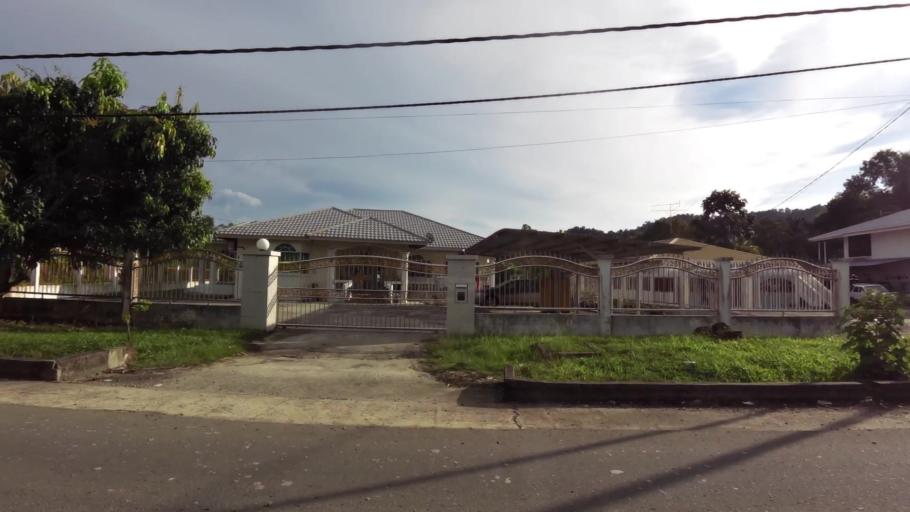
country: BN
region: Brunei and Muara
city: Bandar Seri Begawan
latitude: 4.9556
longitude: 115.0240
